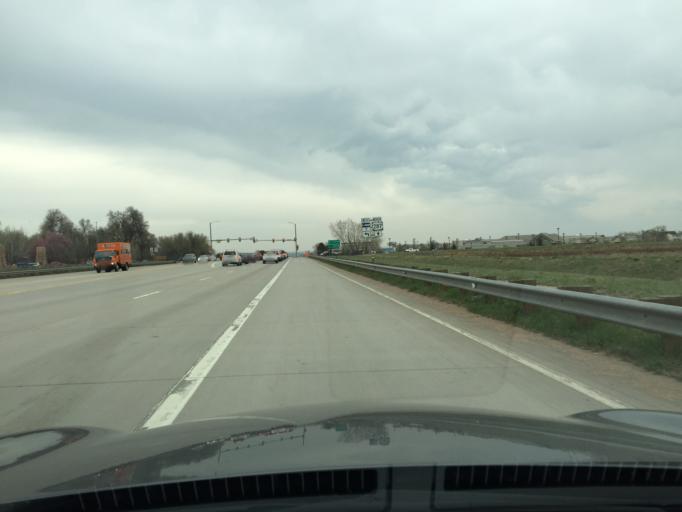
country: US
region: Colorado
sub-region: Boulder County
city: Lafayette
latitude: 40.0131
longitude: -105.1028
